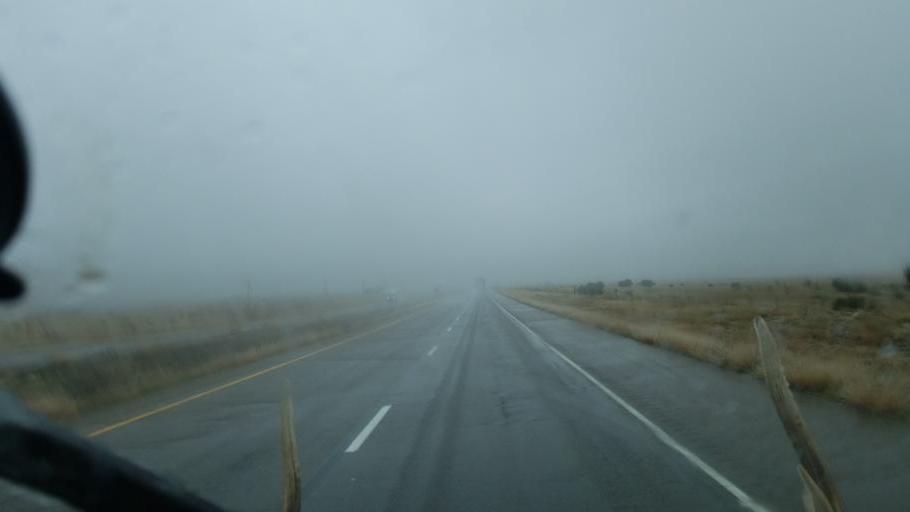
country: US
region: Colorado
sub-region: Pueblo County
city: Colorado City
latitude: 38.0820
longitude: -104.7028
